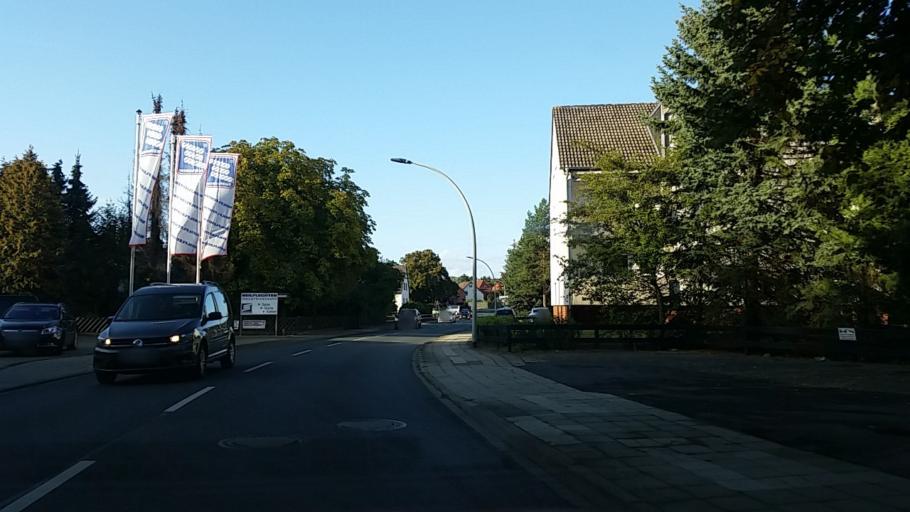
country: DE
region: Lower Saxony
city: Vordorf
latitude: 52.3194
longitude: 10.5256
